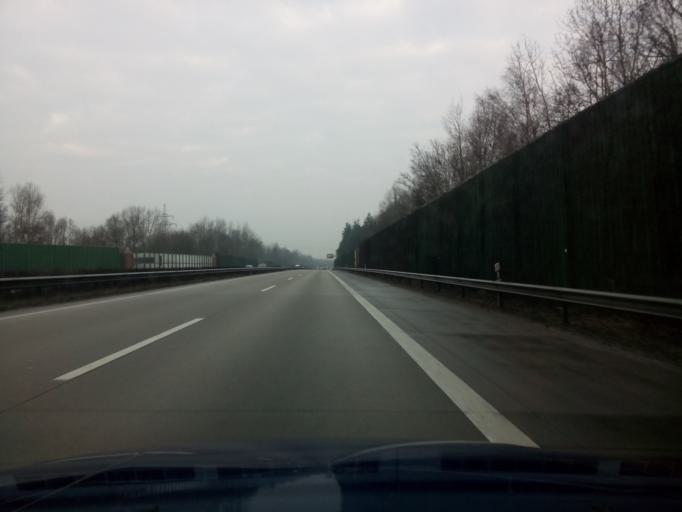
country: DE
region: Lower Saxony
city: Schiffdorf
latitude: 53.5276
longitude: 8.6236
